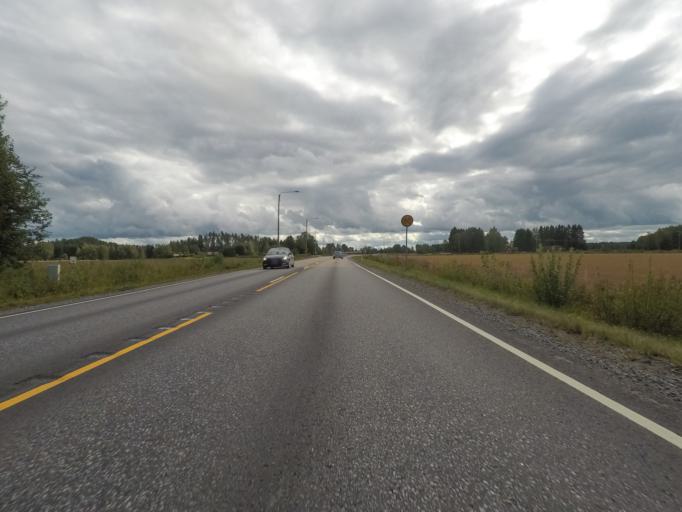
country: FI
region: Paijanne Tavastia
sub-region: Lahti
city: Hartola
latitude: 61.6086
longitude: 26.0081
